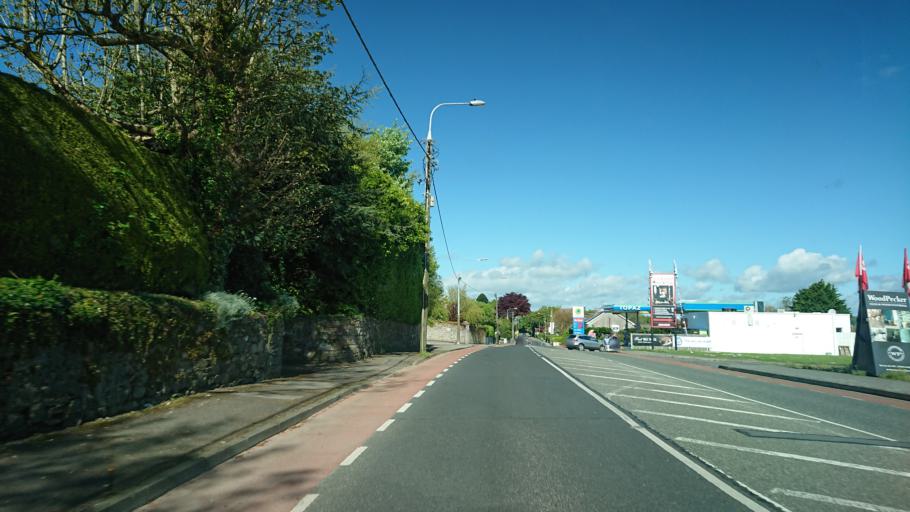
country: IE
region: Munster
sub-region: Waterford
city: Waterford
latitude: 52.2481
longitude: -7.0870
